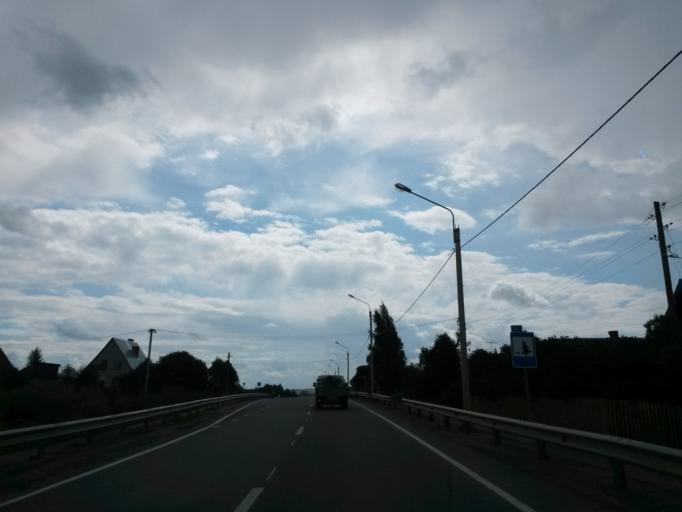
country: RU
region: Jaroslavl
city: Gavrilov-Yam
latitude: 57.3491
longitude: 39.9090
